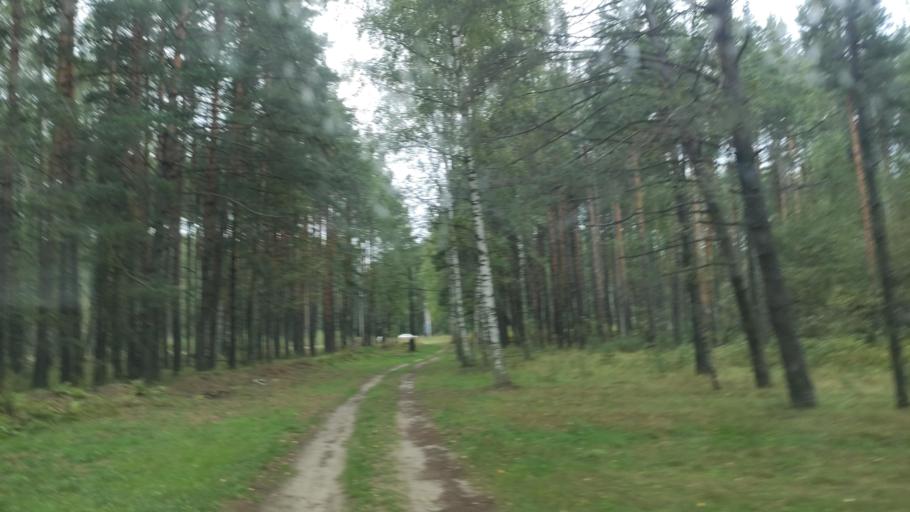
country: RU
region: Nizjnij Novgorod
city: Taremskoye
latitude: 56.0027
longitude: 42.9819
